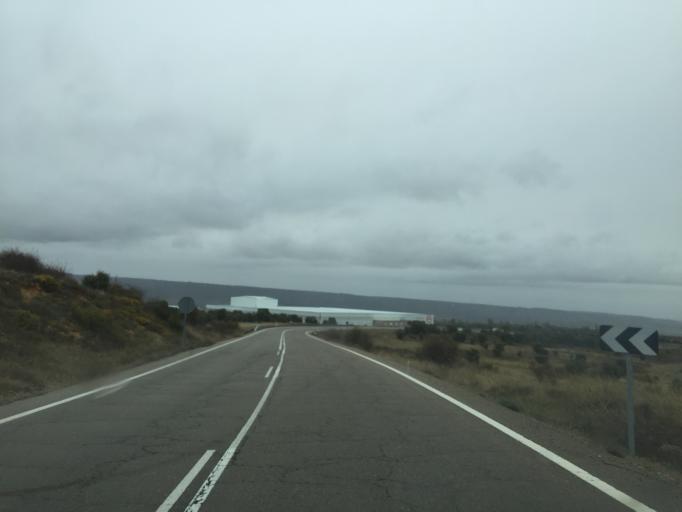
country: ES
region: Castille and Leon
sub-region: Provincia de Leon
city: Cuadros
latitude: 42.6925
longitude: -5.6728
